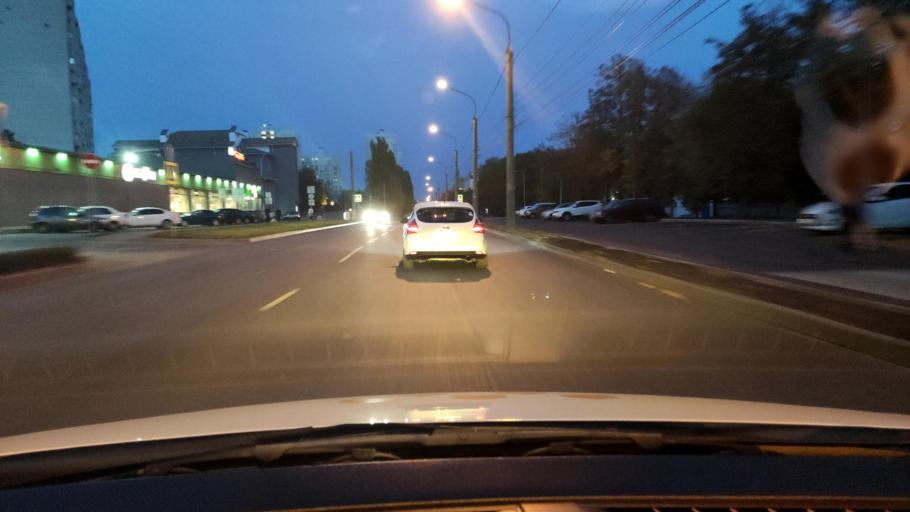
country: RU
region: Voronezj
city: Podgornoye
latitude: 51.6932
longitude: 39.1376
